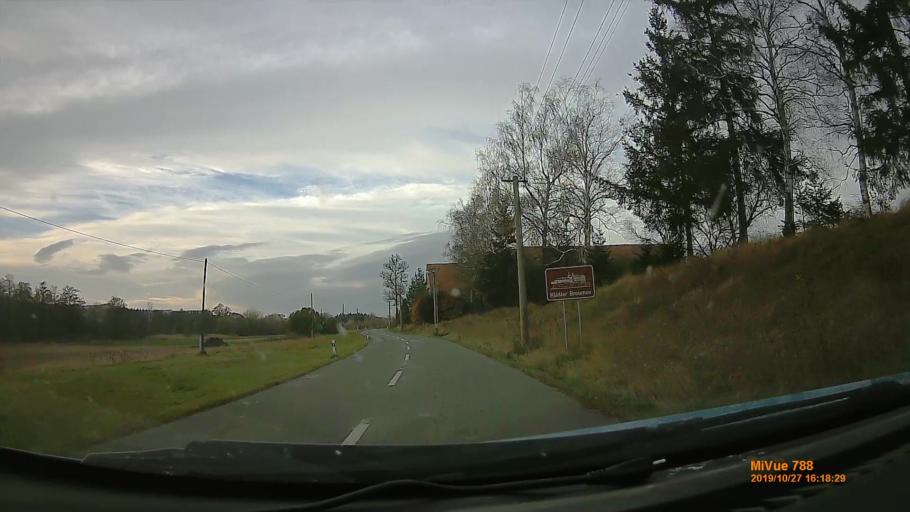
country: CZ
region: Kralovehradecky
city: Broumov
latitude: 50.5672
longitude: 16.3527
